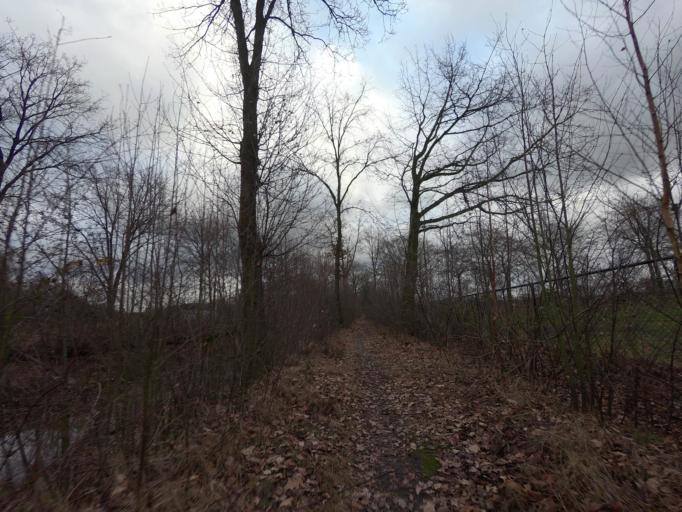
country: BE
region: Flanders
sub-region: Provincie Antwerpen
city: Stabroek
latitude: 51.3474
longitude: 4.4078
